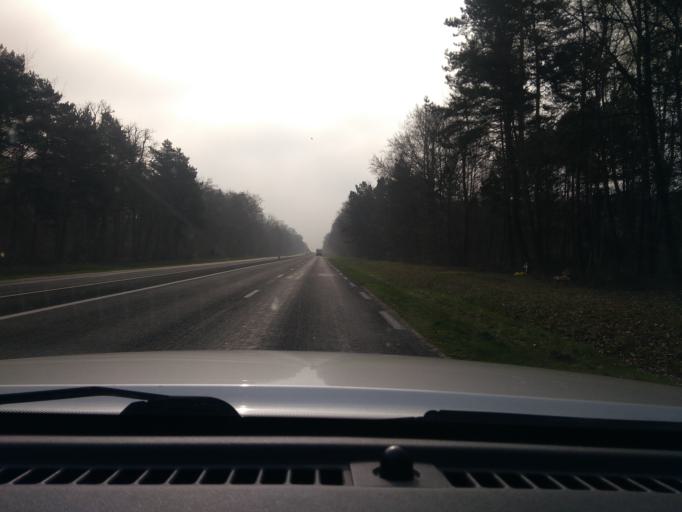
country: FR
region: Ile-de-France
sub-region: Departement de Seine-et-Marne
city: Thomery
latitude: 48.3867
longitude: 2.7627
